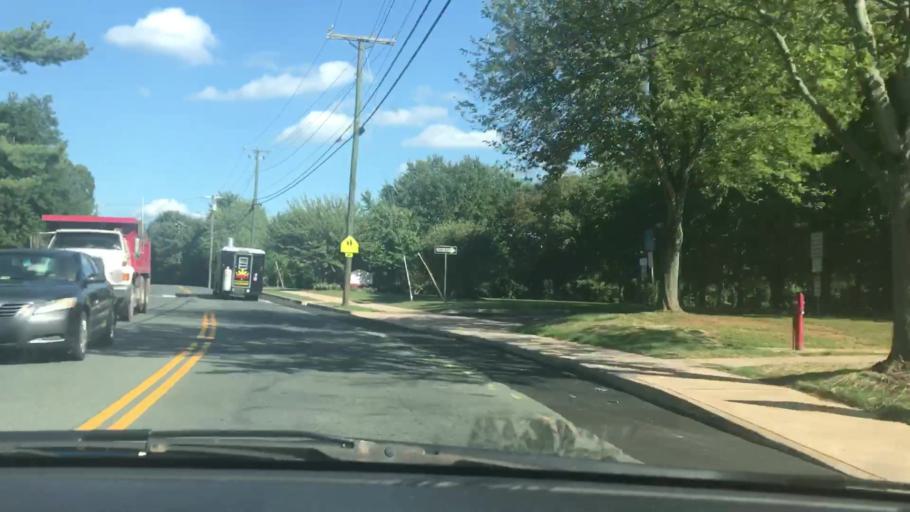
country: US
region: Virginia
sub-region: City of Charlottesville
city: Charlottesville
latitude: 38.0152
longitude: -78.5041
